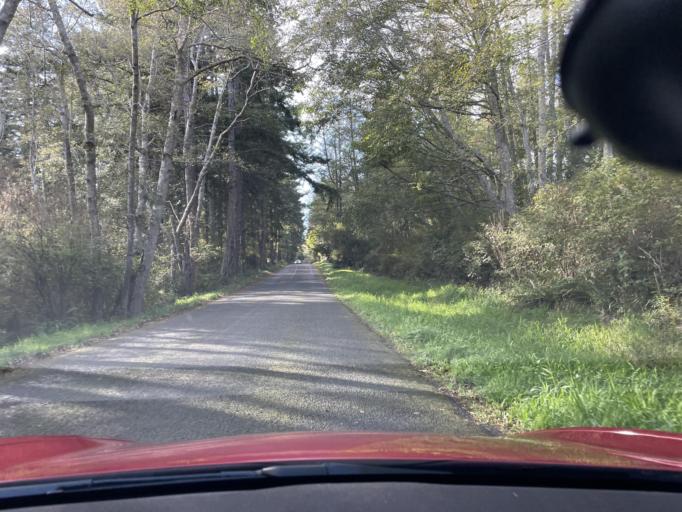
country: US
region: Washington
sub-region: San Juan County
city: Friday Harbor
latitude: 48.4818
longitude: -123.0375
